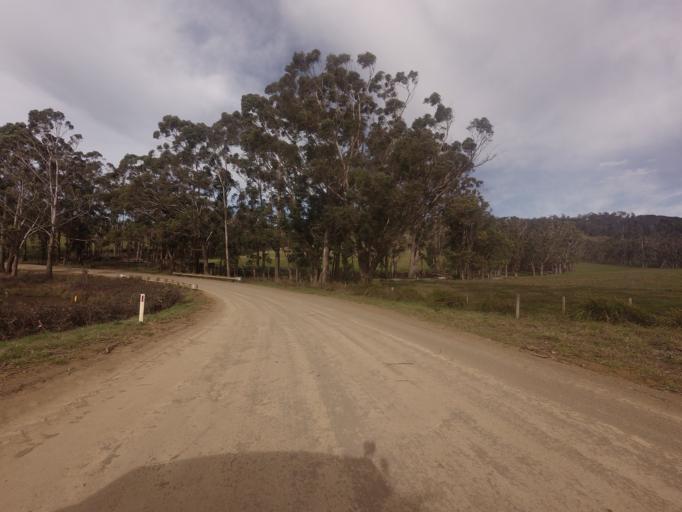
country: AU
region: Tasmania
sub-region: Huon Valley
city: Huonville
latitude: -43.0755
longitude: 147.0584
